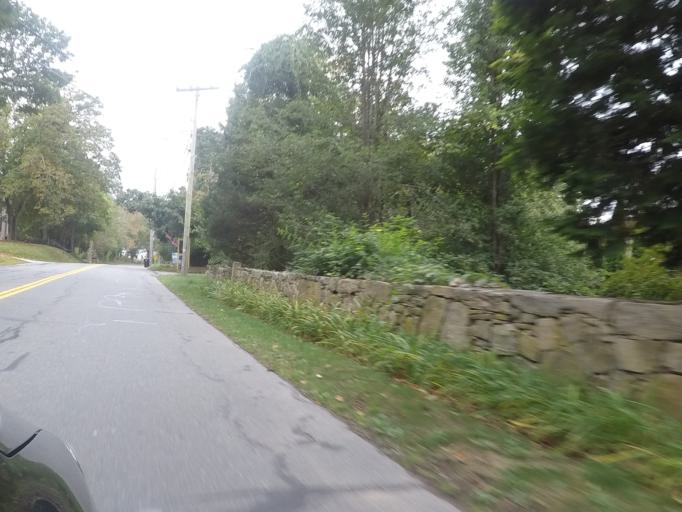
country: US
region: Massachusetts
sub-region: Bristol County
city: Smith Mills
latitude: 41.5753
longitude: -71.0033
